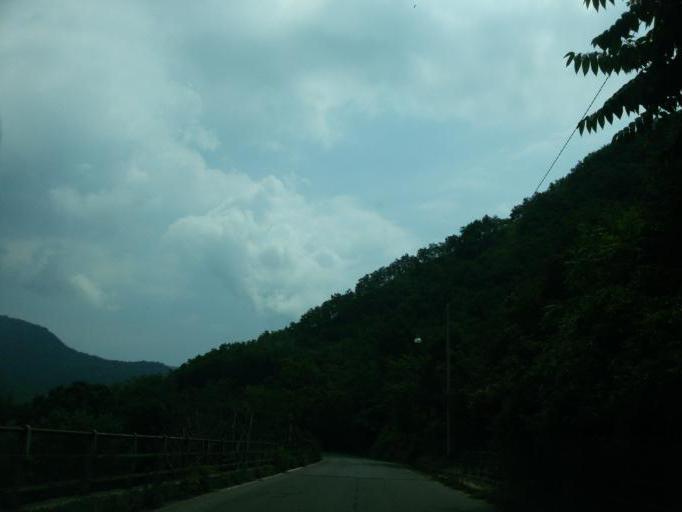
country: IT
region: Liguria
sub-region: Provincia di Genova
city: Piccarello
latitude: 44.4350
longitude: 9.0145
